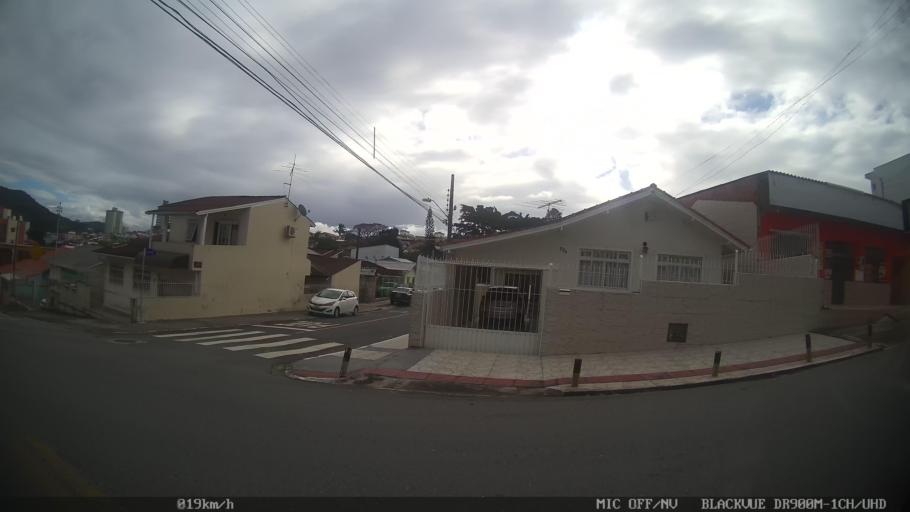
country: BR
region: Santa Catarina
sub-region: Sao Jose
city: Campinas
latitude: -27.5719
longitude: -48.6200
